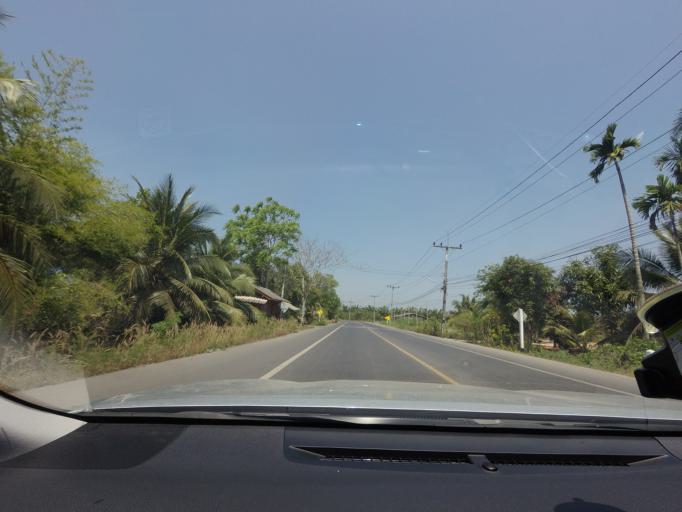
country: TH
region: Surat Thani
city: Phunphin
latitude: 9.1955
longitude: 99.2477
